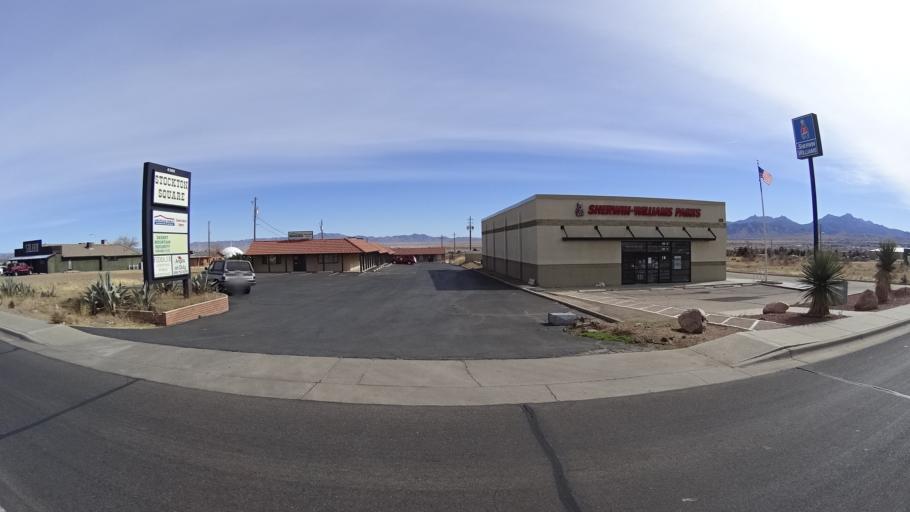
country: US
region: Arizona
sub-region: Mohave County
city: New Kingman-Butler
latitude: 35.2507
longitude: -114.0389
